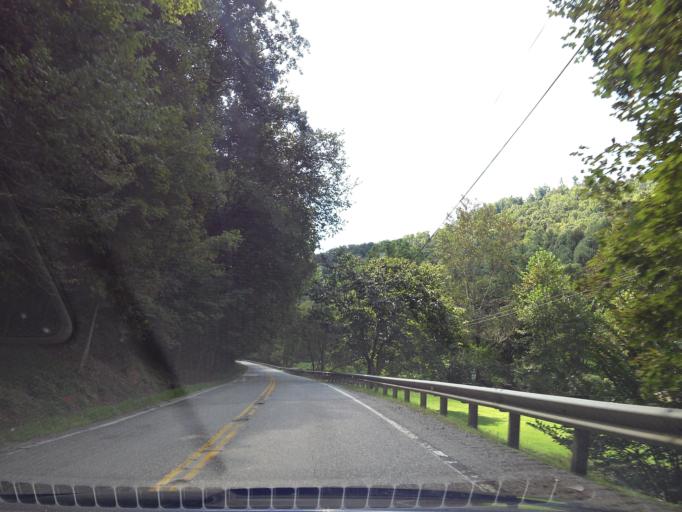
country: US
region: Kentucky
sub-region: Harlan County
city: Loyall
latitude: 36.9513
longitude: -83.3923
